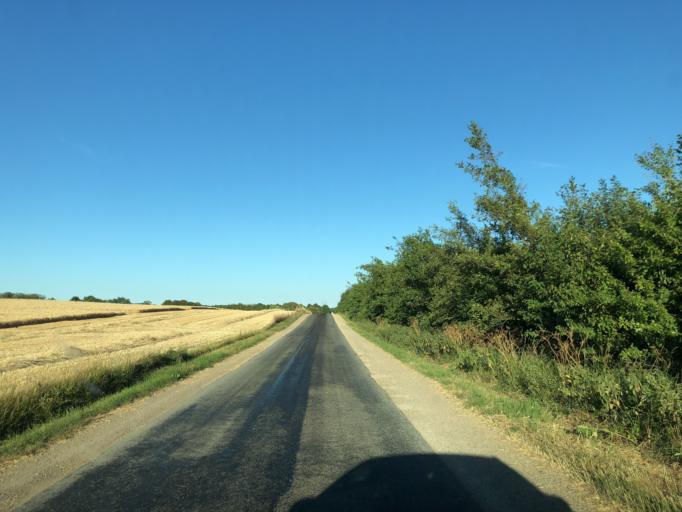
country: DK
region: Central Jutland
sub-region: Horsens Kommune
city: Horsens
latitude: 55.9214
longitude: 9.8854
